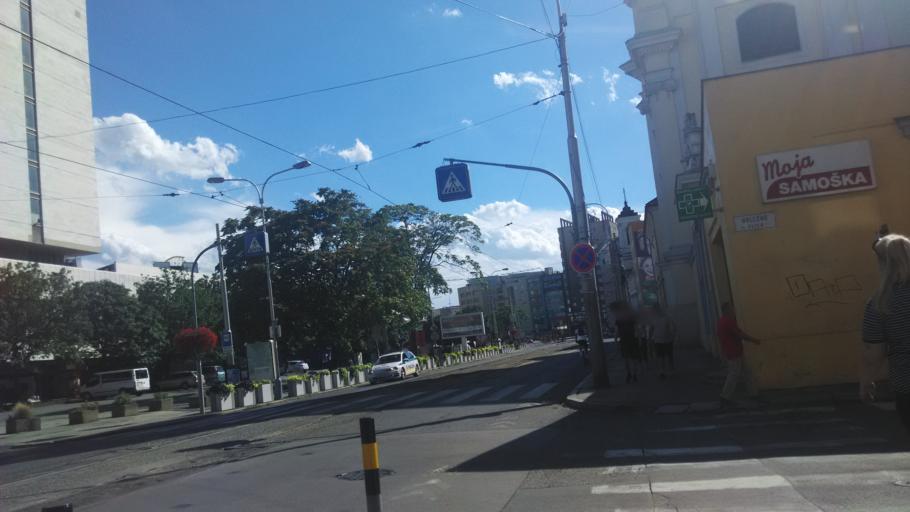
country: SK
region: Bratislavsky
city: Bratislava
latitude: 48.1471
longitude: 17.1149
